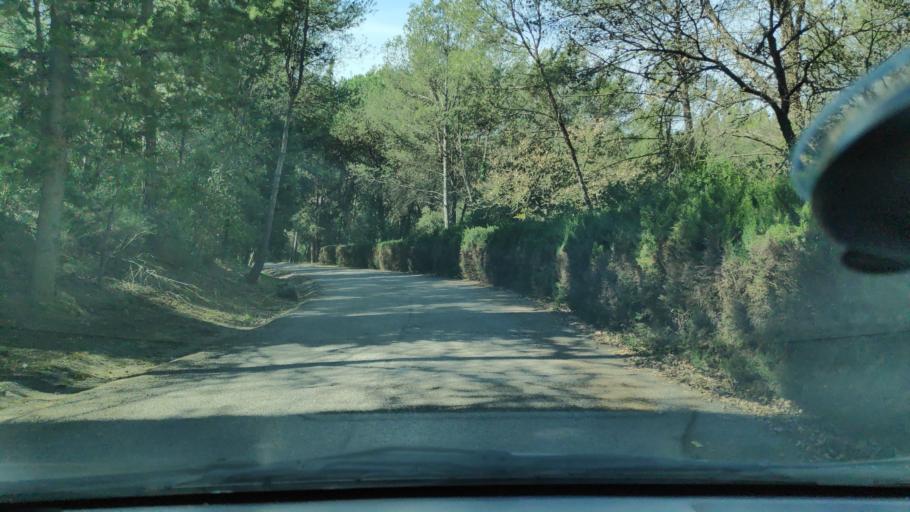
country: ES
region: Catalonia
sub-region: Provincia de Barcelona
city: Rubi
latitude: 41.5119
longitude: 2.0521
